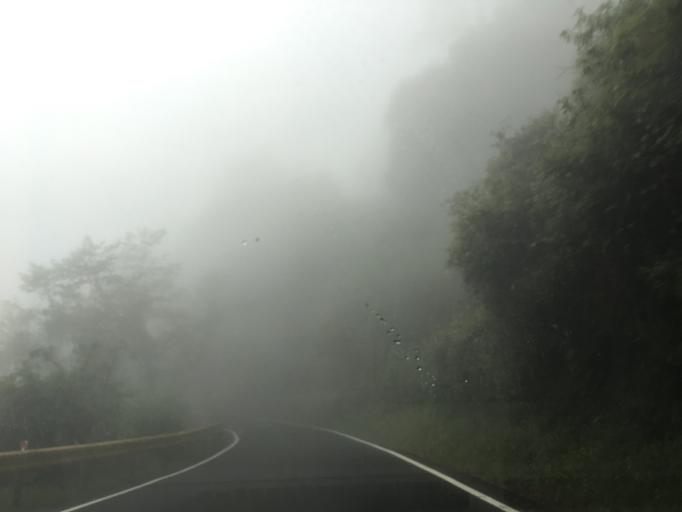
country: TW
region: Taiwan
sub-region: Hualien
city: Hualian
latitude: 24.1967
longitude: 121.4257
